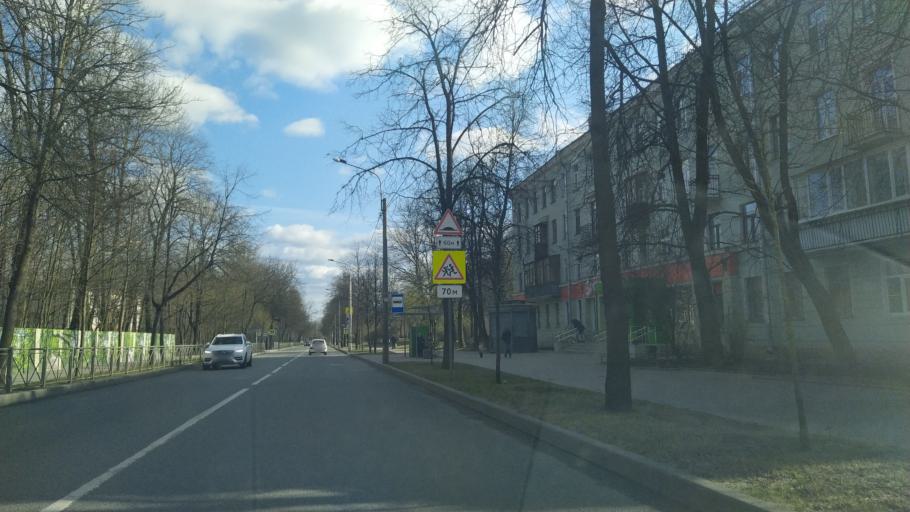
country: RU
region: St.-Petersburg
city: Pushkin
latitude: 59.7076
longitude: 30.4156
